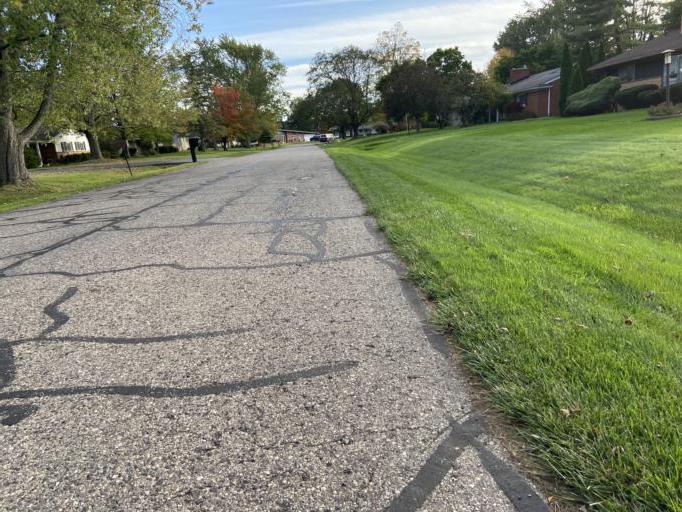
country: US
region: Michigan
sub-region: Oakland County
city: Farmington Hills
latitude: 42.5101
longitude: -83.3611
